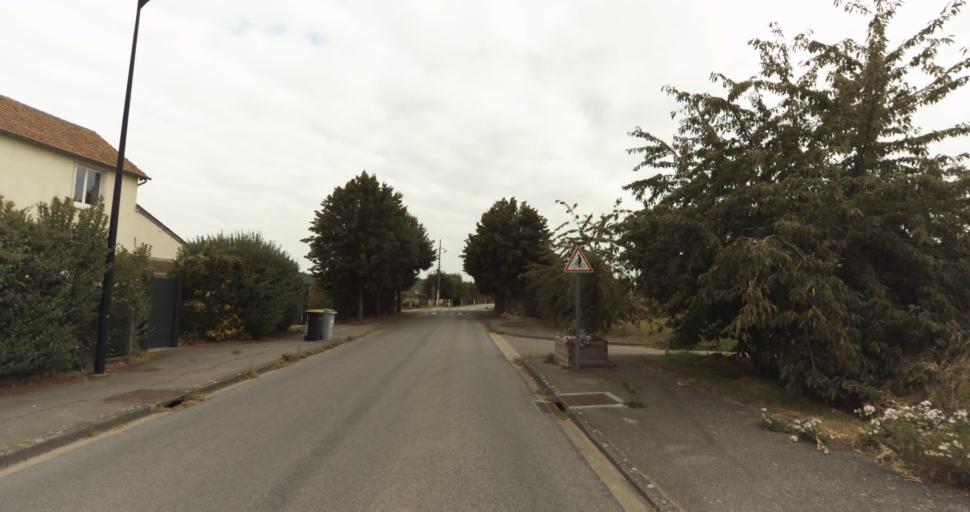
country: FR
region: Haute-Normandie
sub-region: Departement de l'Eure
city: Marcilly-sur-Eure
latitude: 48.8296
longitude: 1.3478
